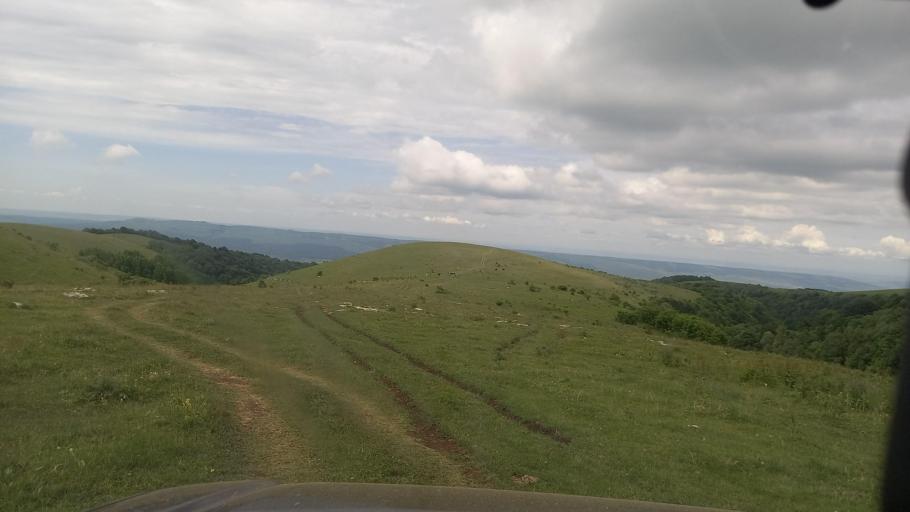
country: RU
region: Karachayevo-Cherkesiya
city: Pregradnaya
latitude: 43.9987
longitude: 41.2729
